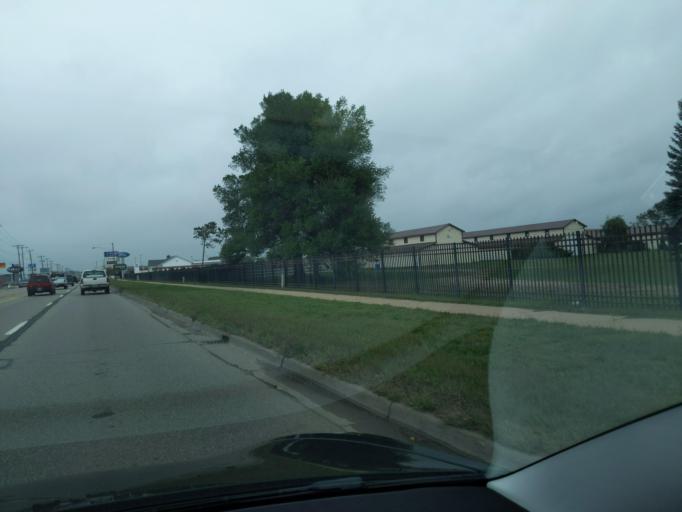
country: US
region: Michigan
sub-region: Wexford County
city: Cadillac
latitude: 44.2687
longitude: -85.4064
